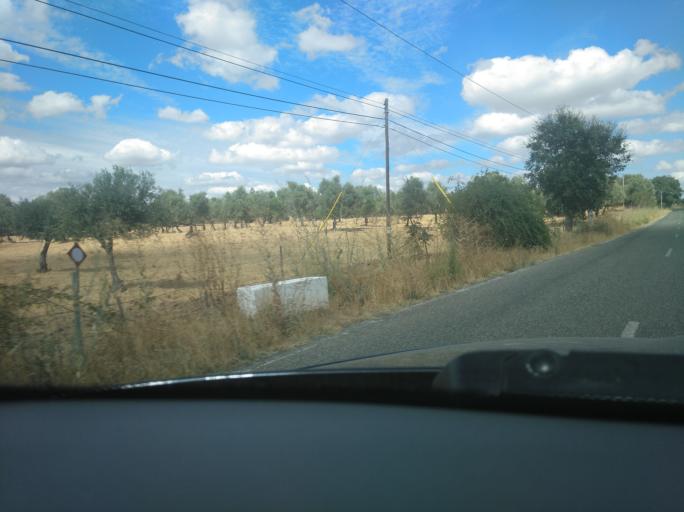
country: PT
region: Portalegre
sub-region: Arronches
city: Arronches
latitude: 39.0573
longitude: -7.4247
